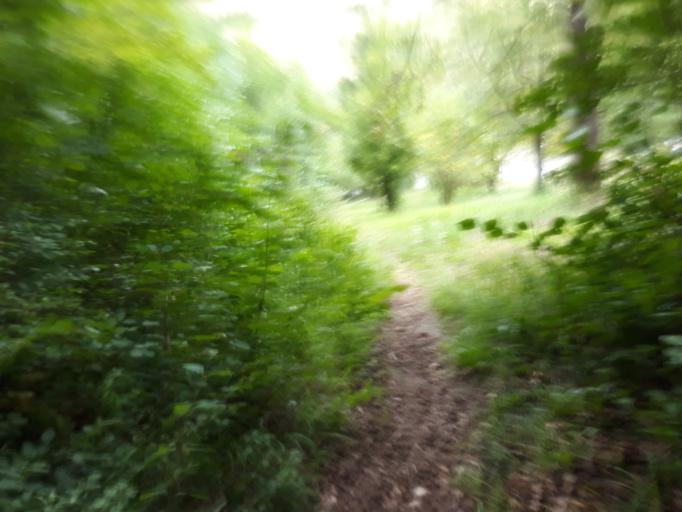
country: DE
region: Baden-Wuerttemberg
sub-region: Regierungsbezirk Stuttgart
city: Schonaich
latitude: 48.6667
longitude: 9.0494
